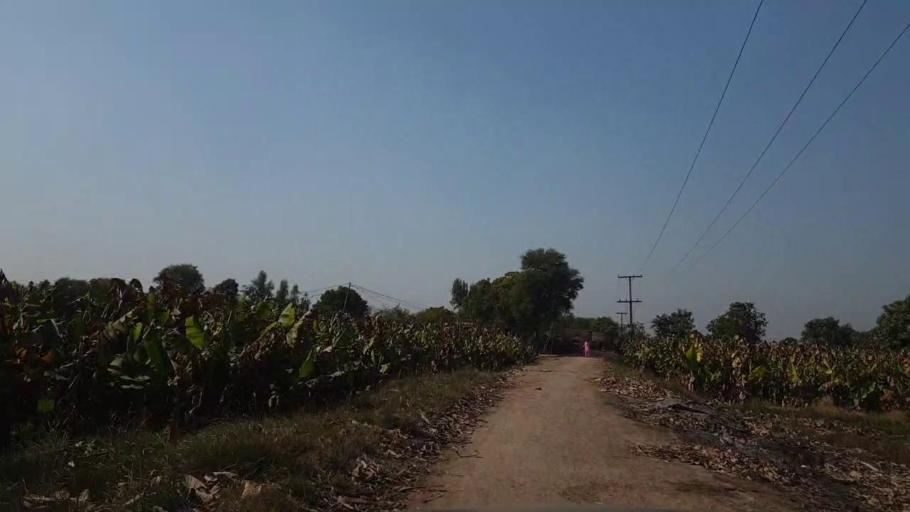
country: PK
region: Sindh
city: Tando Allahyar
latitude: 25.5457
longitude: 68.6790
